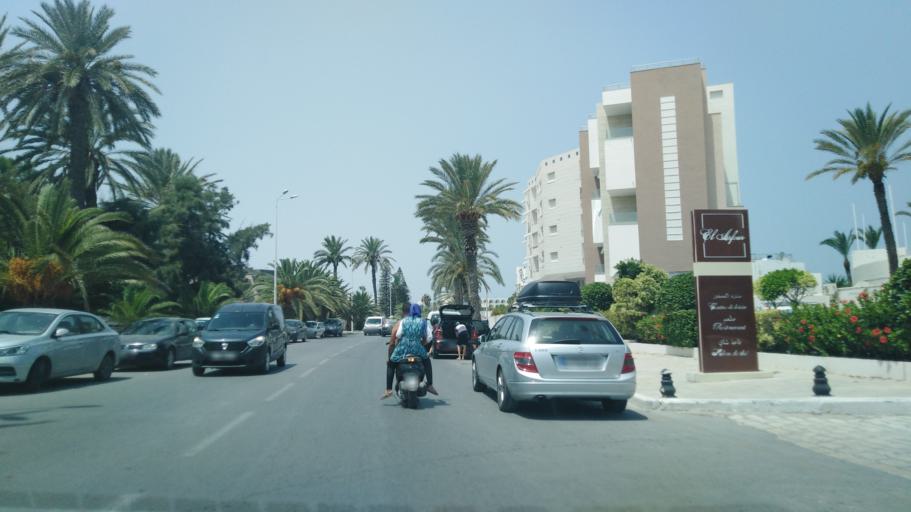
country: TN
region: Al Mahdiyah
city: Mahdia
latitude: 35.5131
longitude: 11.0480
